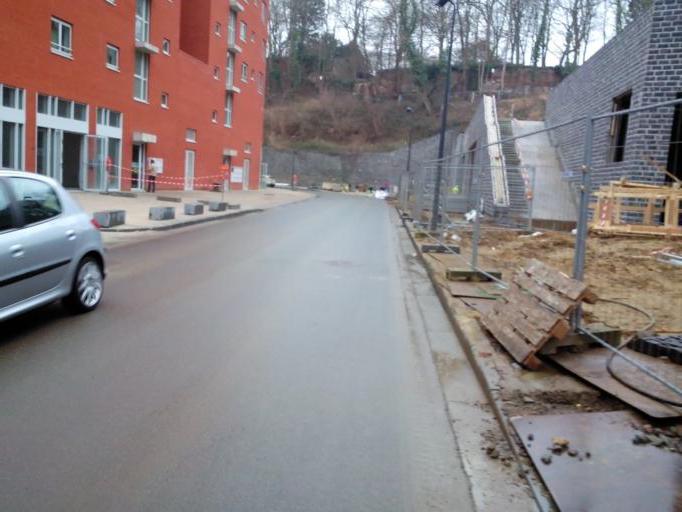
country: BE
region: Flanders
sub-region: Provincie Vlaams-Brabant
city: Leuven
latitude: 50.8887
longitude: 4.7016
